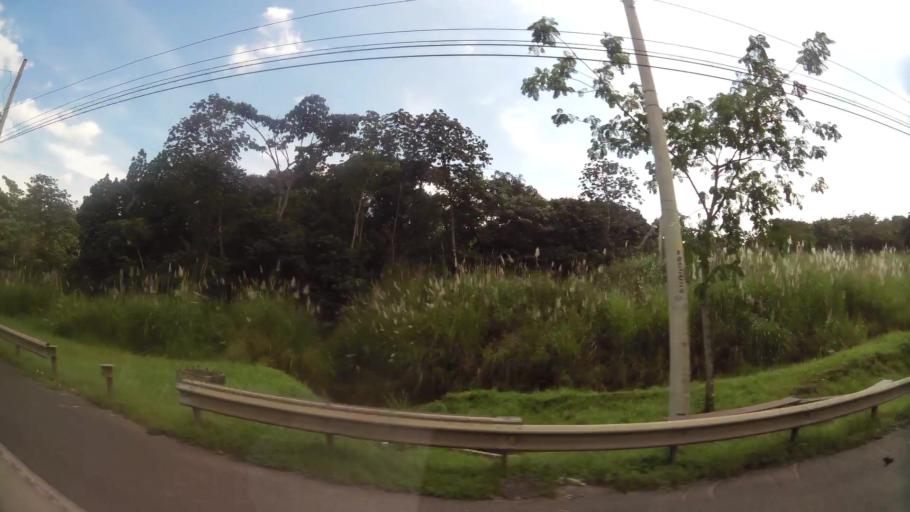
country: PA
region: Panama
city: Las Cumbres
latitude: 9.0409
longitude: -79.5620
